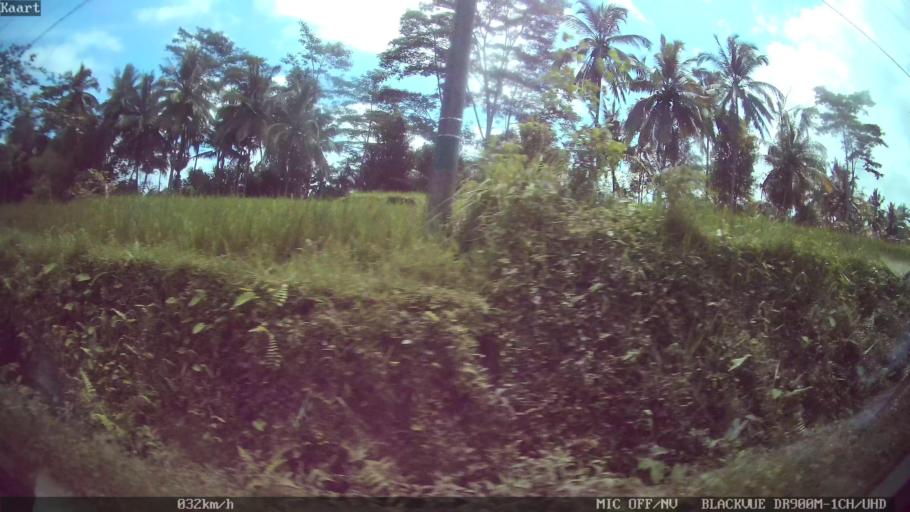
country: ID
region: Bali
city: Banjar Apuan Kaja
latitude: -8.4992
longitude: 115.3409
